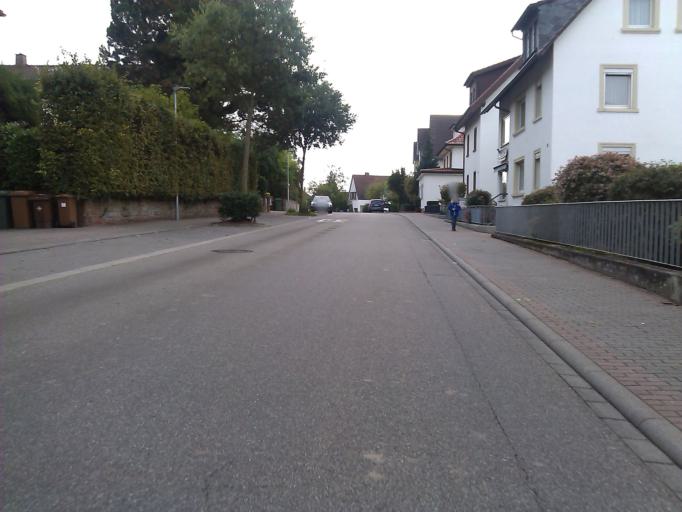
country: DE
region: Baden-Wuerttemberg
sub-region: Karlsruhe Region
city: Weinheim
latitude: 49.5324
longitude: 8.6654
